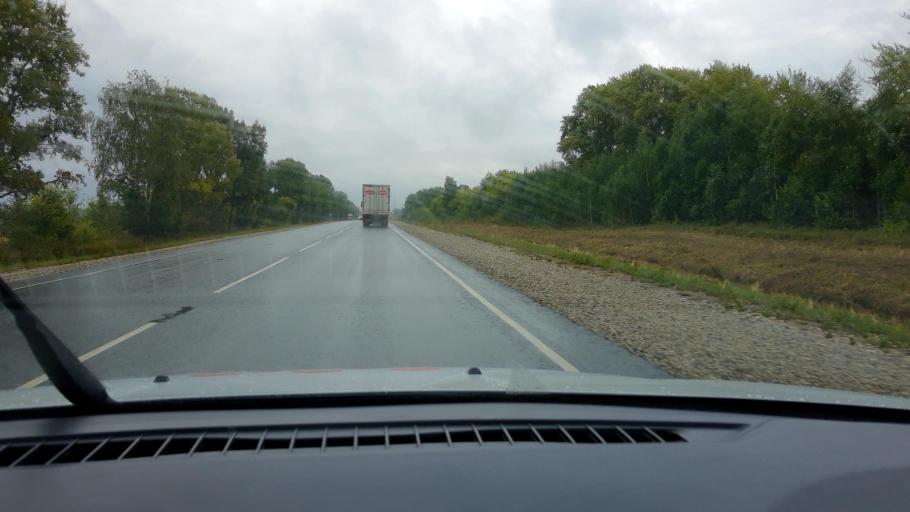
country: RU
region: Chuvashia
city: Tsivil'sk
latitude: 55.7901
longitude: 47.6839
